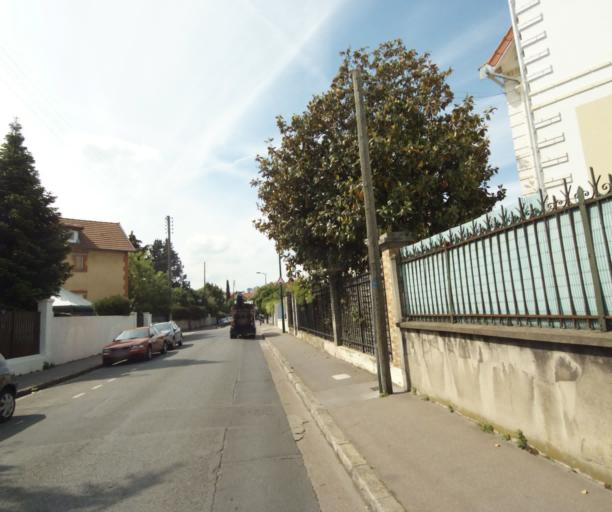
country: FR
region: Ile-de-France
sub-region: Departement des Hauts-de-Seine
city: La Garenne-Colombes
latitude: 48.9150
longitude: 2.2420
